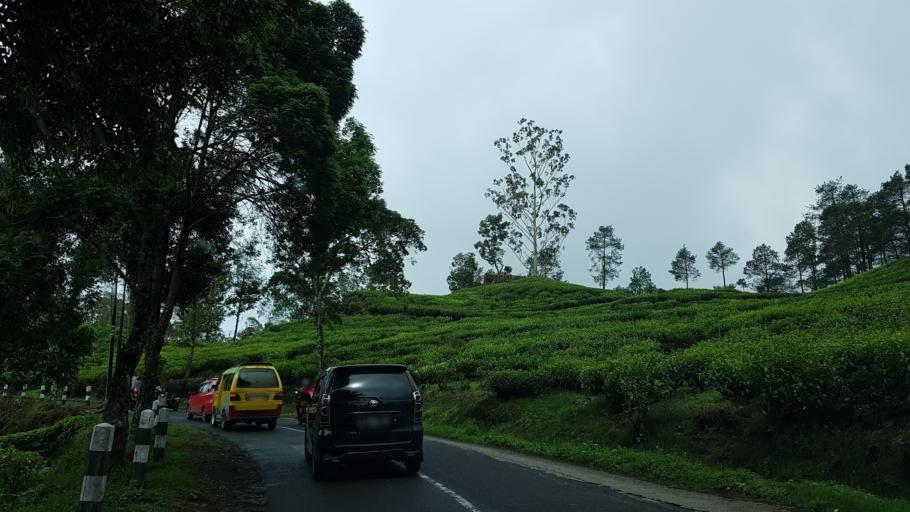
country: ID
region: West Java
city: Banjar
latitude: -7.1463
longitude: 107.3862
